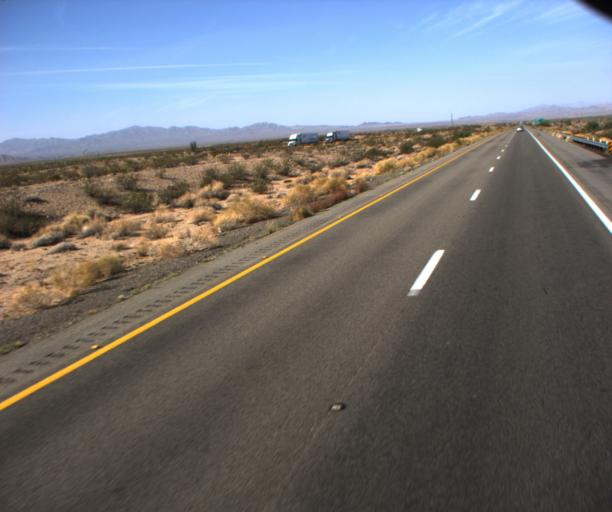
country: US
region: Arizona
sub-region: Mohave County
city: Desert Hills
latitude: 34.7898
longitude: -114.1682
